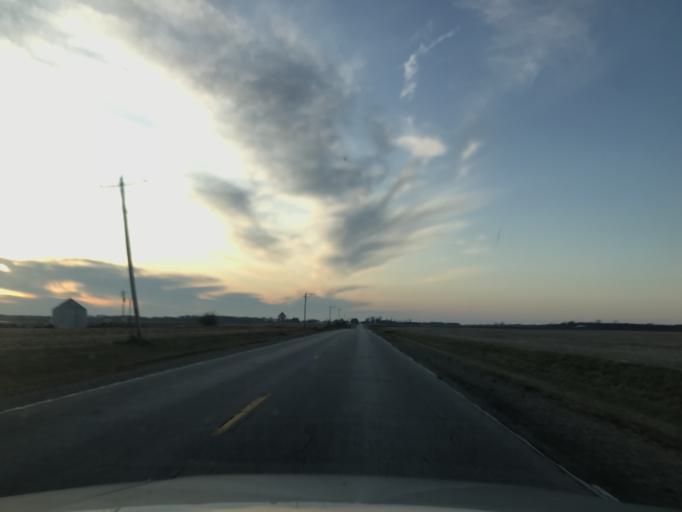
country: US
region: Illinois
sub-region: Warren County
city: Monmouth
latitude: 41.0247
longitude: -90.7493
